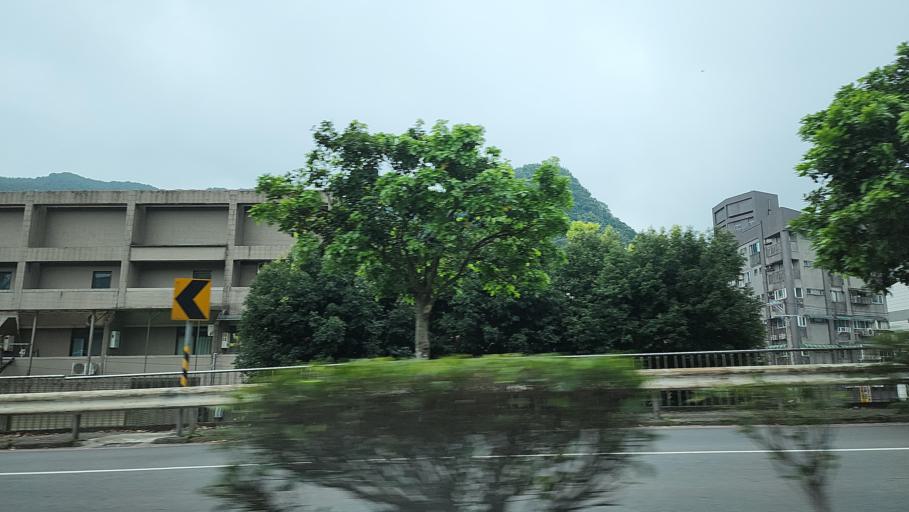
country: TW
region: Taiwan
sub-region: Keelung
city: Keelung
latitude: 25.1582
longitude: 121.6944
